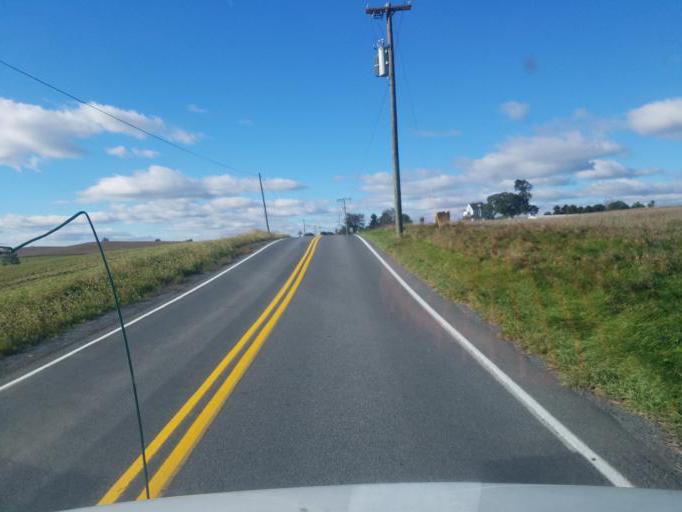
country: US
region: Pennsylvania
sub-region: Franklin County
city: Mont Alto
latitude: 39.8733
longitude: -77.5746
